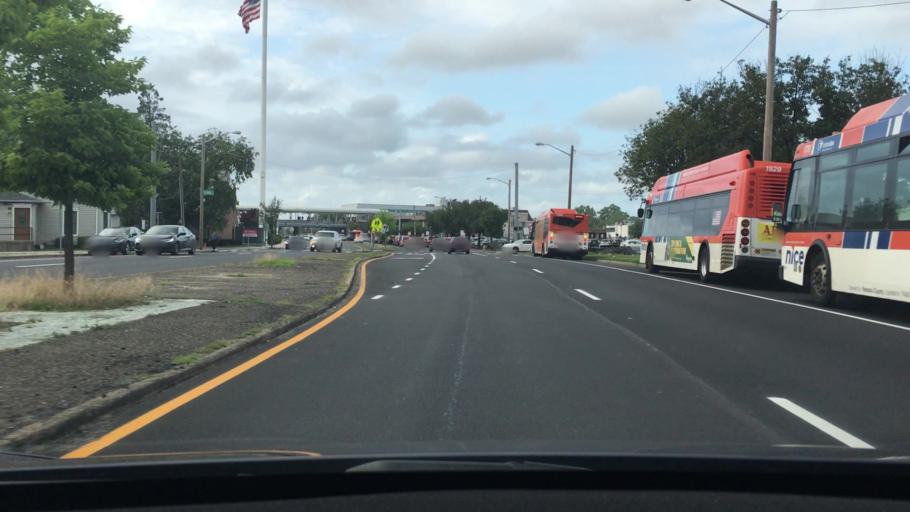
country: US
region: New York
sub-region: Nassau County
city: Hicksville
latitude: 40.7642
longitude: -73.5272
